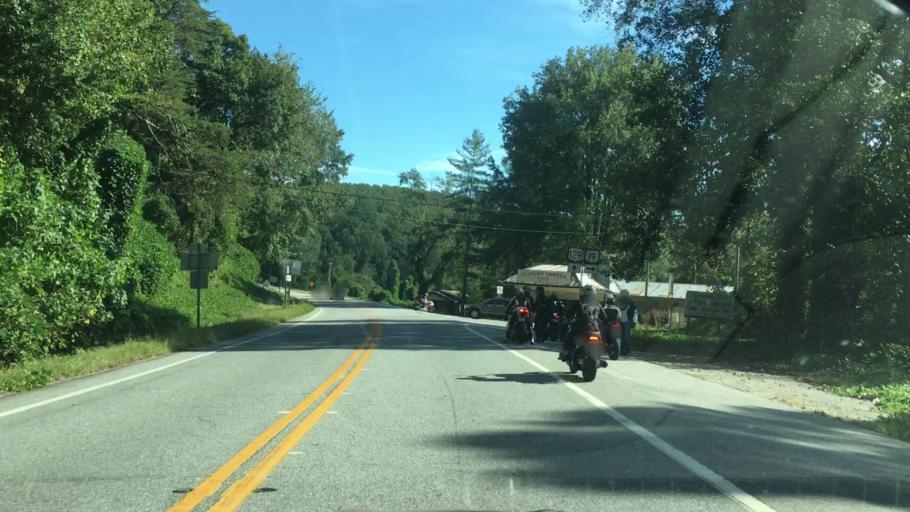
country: US
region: Georgia
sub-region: White County
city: Cleveland
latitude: 34.6636
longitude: -83.9013
